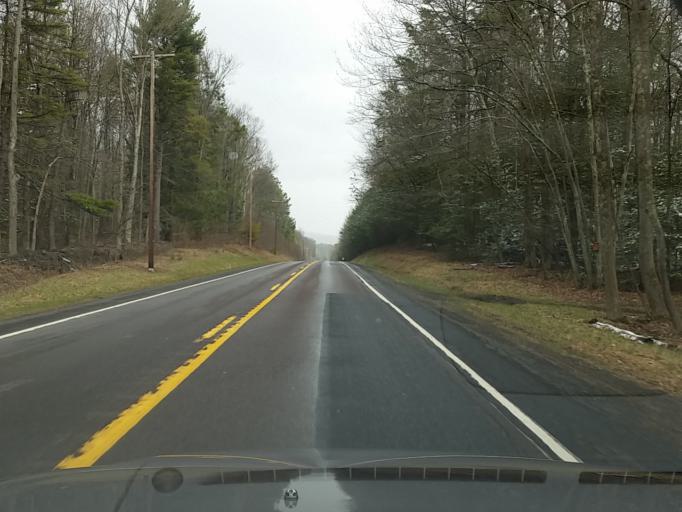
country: US
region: Pennsylvania
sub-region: Sullivan County
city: Laporte
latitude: 41.2781
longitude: -76.4198
